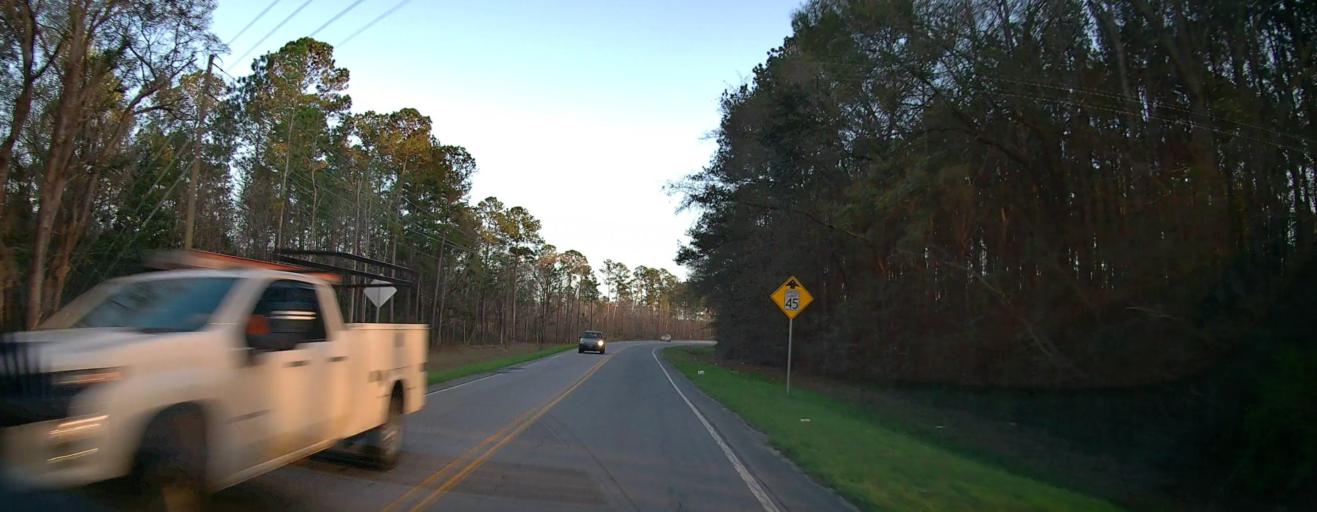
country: US
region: Georgia
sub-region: Chatham County
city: Bloomingdale
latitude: 32.1320
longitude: -81.3873
